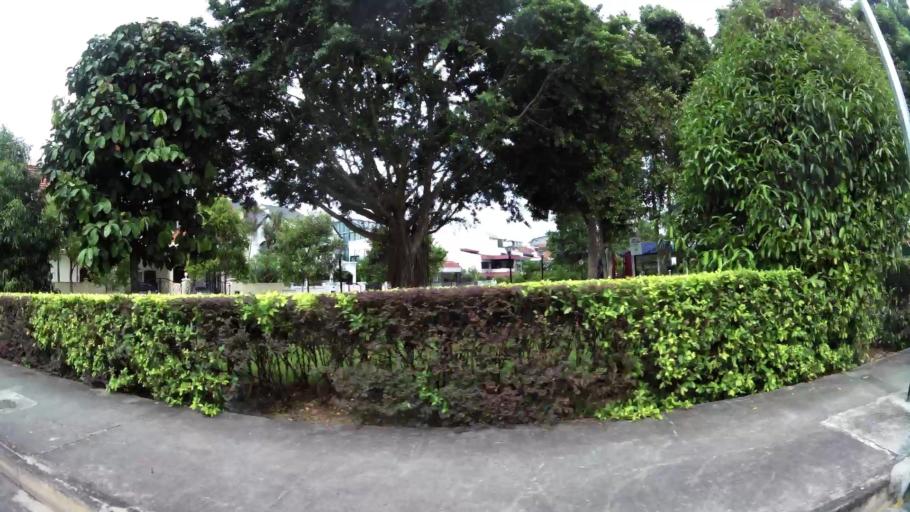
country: SG
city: Singapore
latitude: 1.3220
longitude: 103.7962
